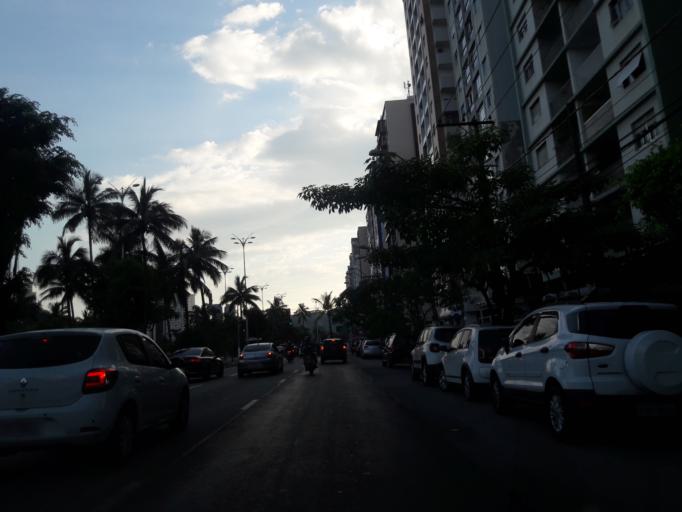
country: BR
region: Sao Paulo
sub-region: Sao Vicente
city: Sao Vicente
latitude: -23.9712
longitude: -46.3691
